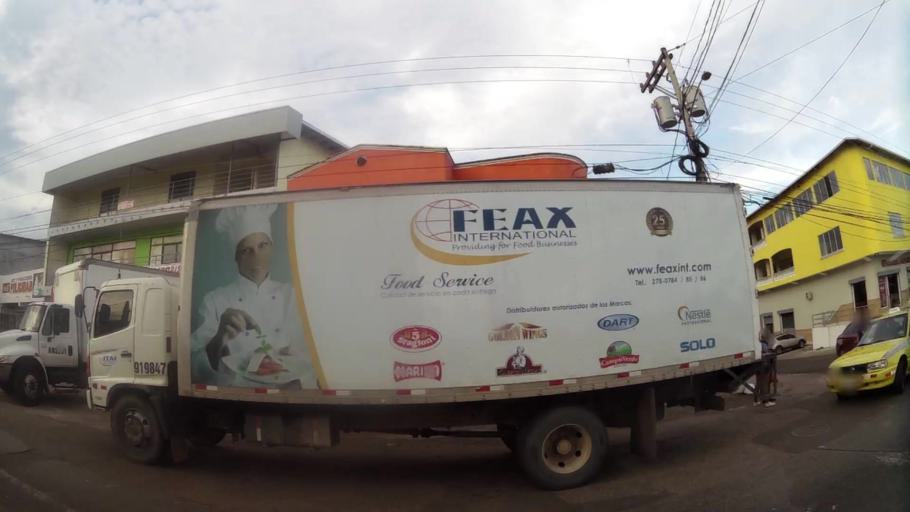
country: PA
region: Panama
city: La Chorrera
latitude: 8.8738
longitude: -79.7764
